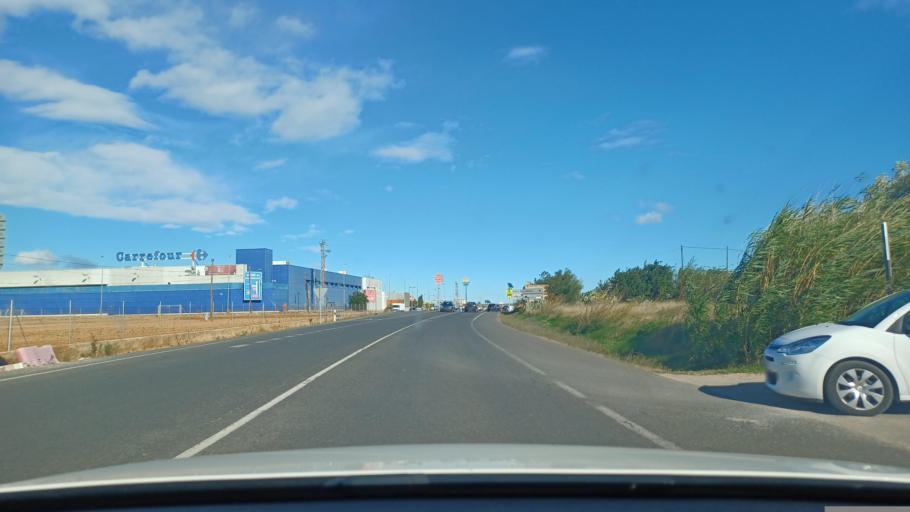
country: ES
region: Valencia
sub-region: Provincia de Castello
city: Vinaros
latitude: 40.4520
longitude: 0.4512
